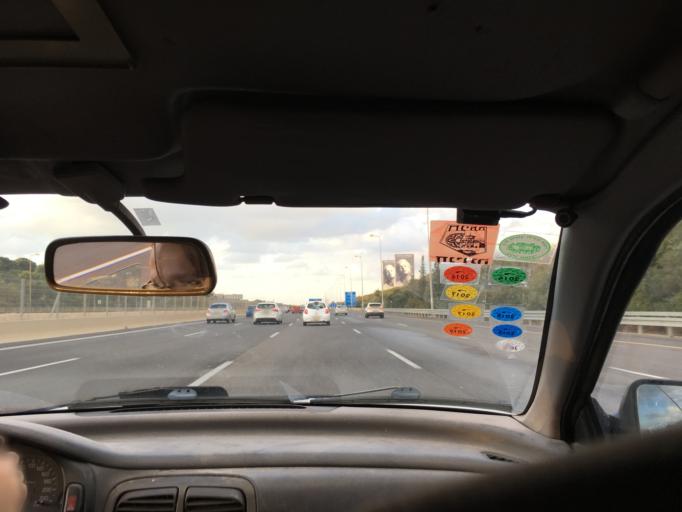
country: IL
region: Tel Aviv
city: Ramat HaSharon
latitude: 32.1223
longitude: 34.8107
